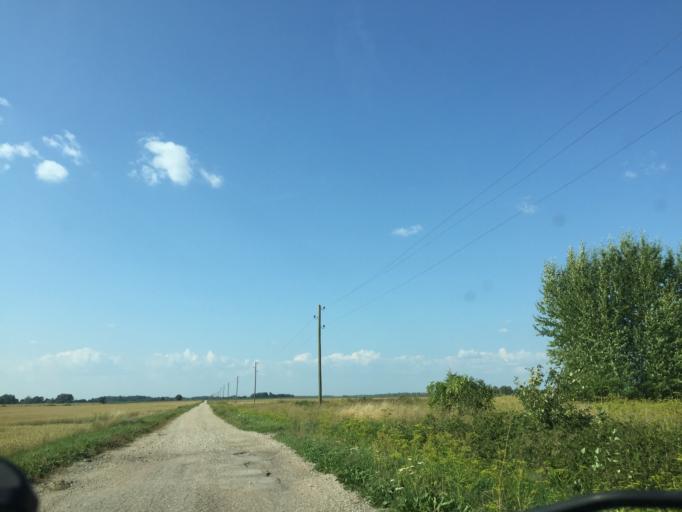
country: LV
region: Jelgava
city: Jelgava
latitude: 56.4557
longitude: 23.6810
